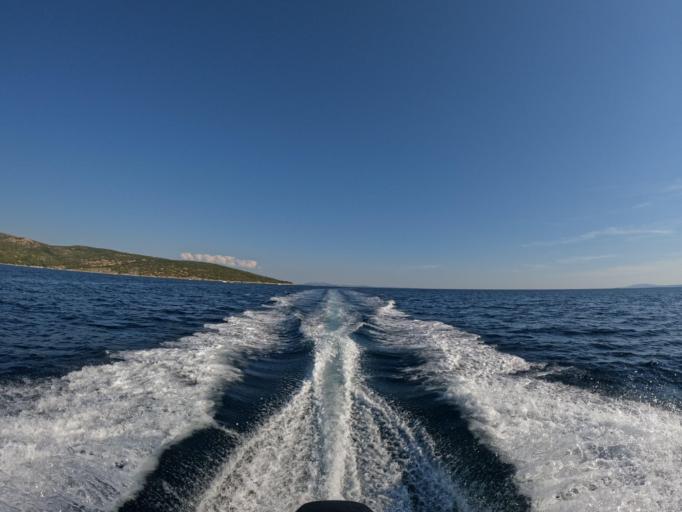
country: HR
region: Primorsko-Goranska
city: Punat
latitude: 44.9918
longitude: 14.6051
